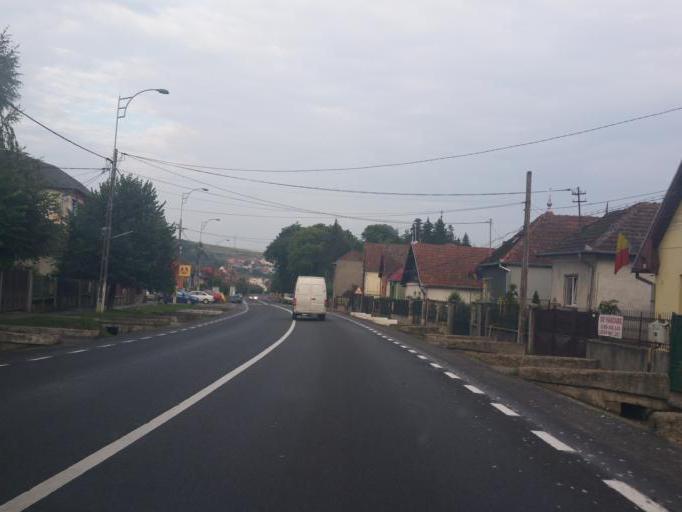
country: RO
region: Cluj
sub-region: Comuna Baciu
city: Baciu
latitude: 46.7973
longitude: 23.5130
